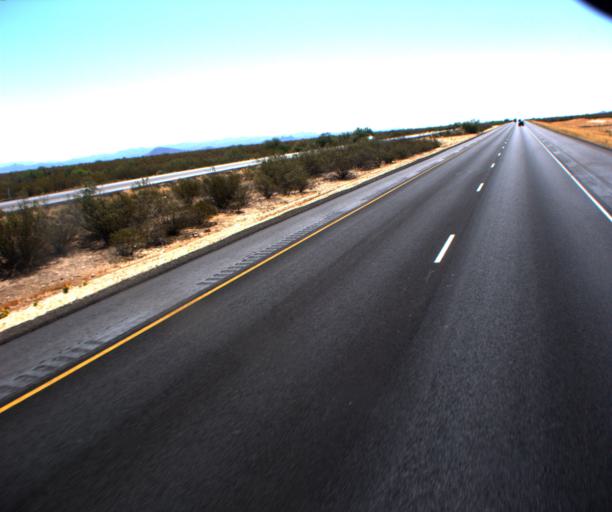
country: US
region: Arizona
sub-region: Yavapai County
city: Congress
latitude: 34.0793
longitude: -112.8877
